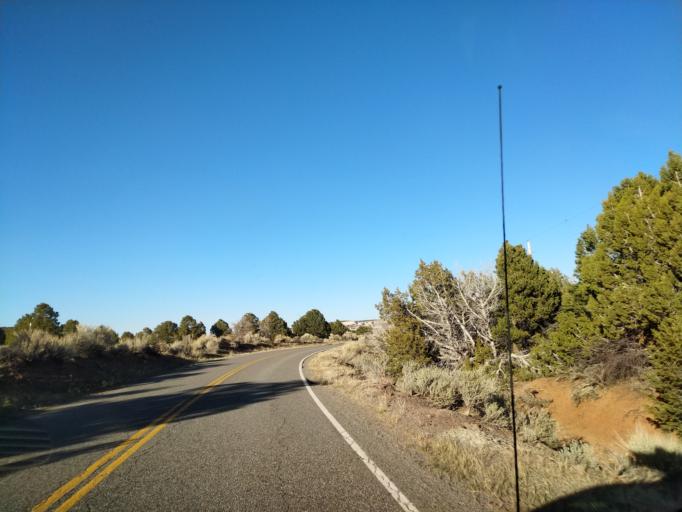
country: US
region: Colorado
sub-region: Mesa County
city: Loma
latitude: 38.9552
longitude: -108.9371
